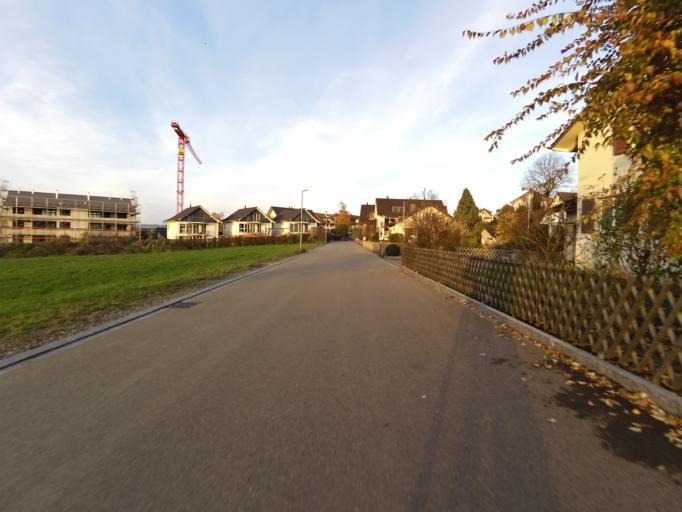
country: CH
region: Thurgau
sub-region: Frauenfeld District
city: Pfyn
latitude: 47.5719
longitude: 8.9441
